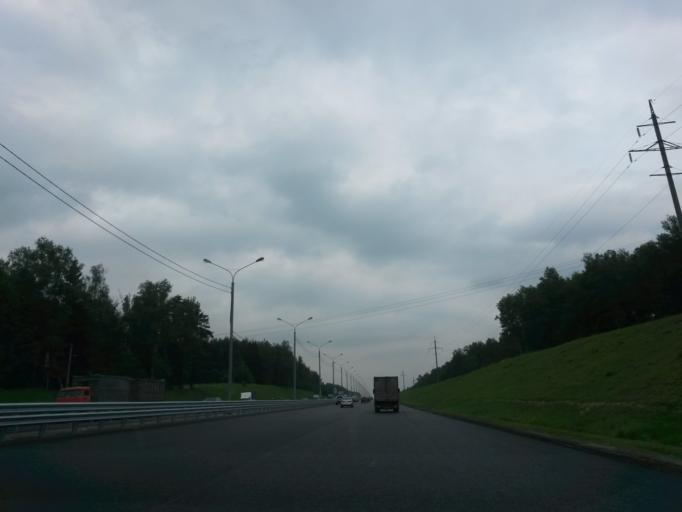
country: RU
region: Moskovskaya
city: Lyubuchany
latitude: 55.2713
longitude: 37.5378
